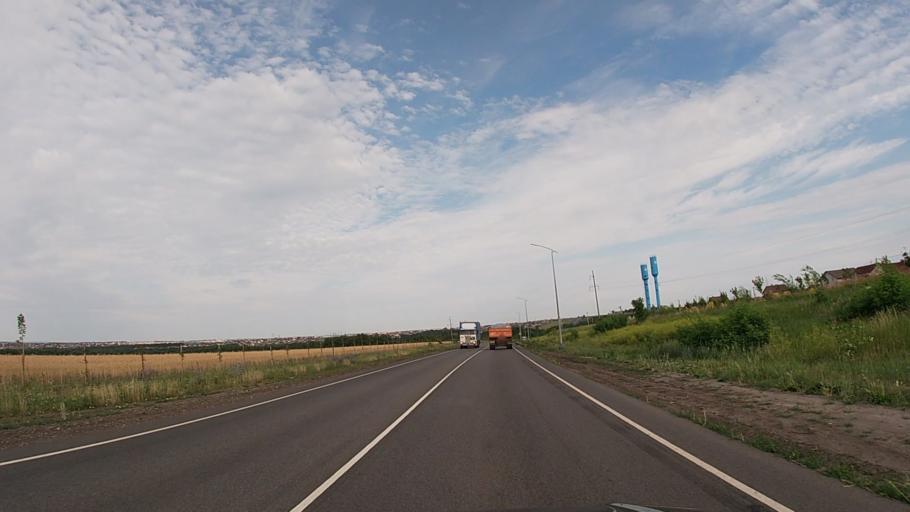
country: RU
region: Belgorod
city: Severnyy
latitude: 50.6655
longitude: 36.4994
